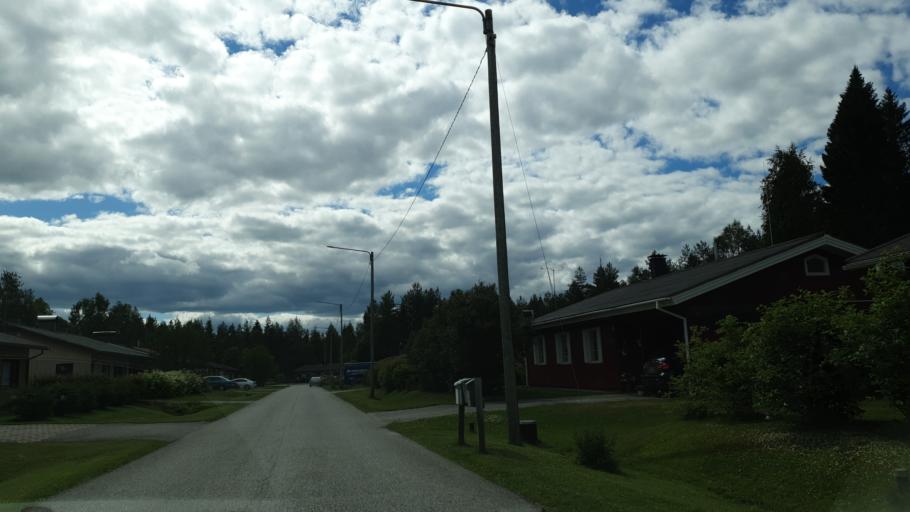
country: FI
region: Kainuu
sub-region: Kehys-Kainuu
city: Kuhmo
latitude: 64.1164
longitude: 29.4785
